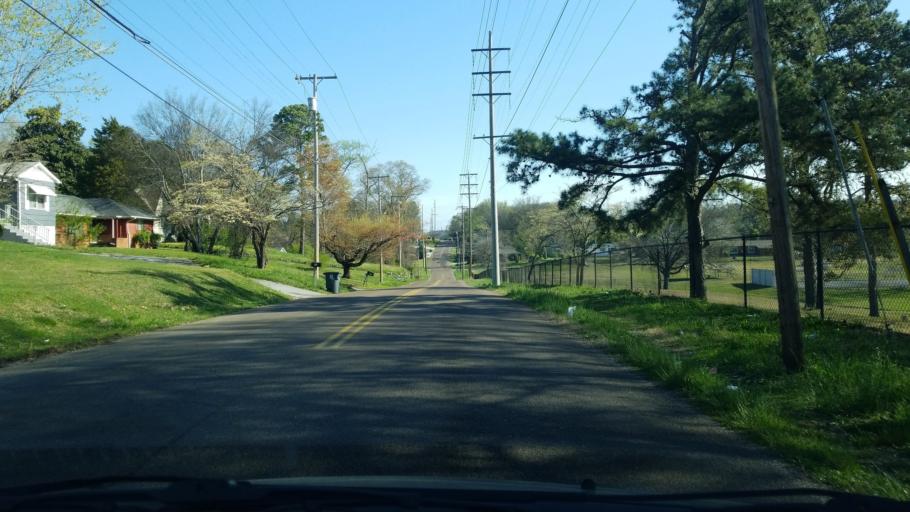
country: US
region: Tennessee
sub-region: Hamilton County
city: East Ridge
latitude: 35.0283
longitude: -85.2442
